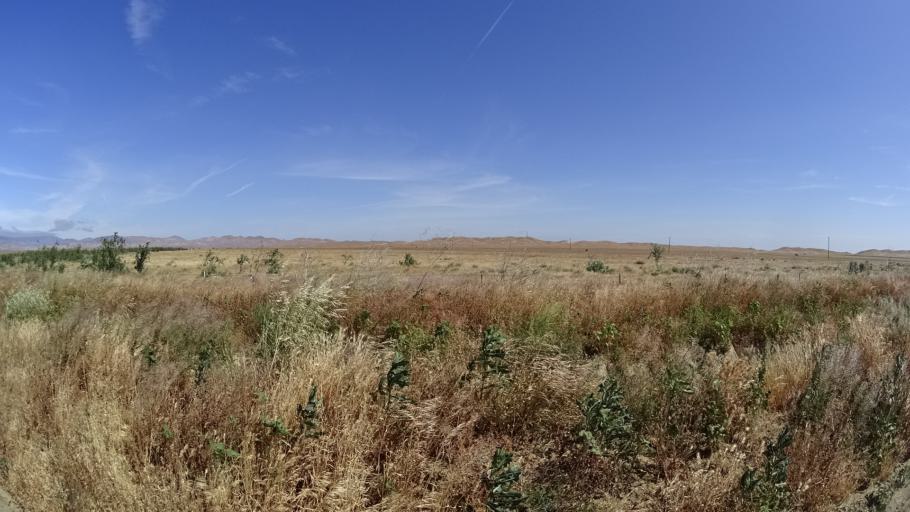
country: US
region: California
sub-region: Kings County
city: Avenal
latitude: 35.8179
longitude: -120.0786
